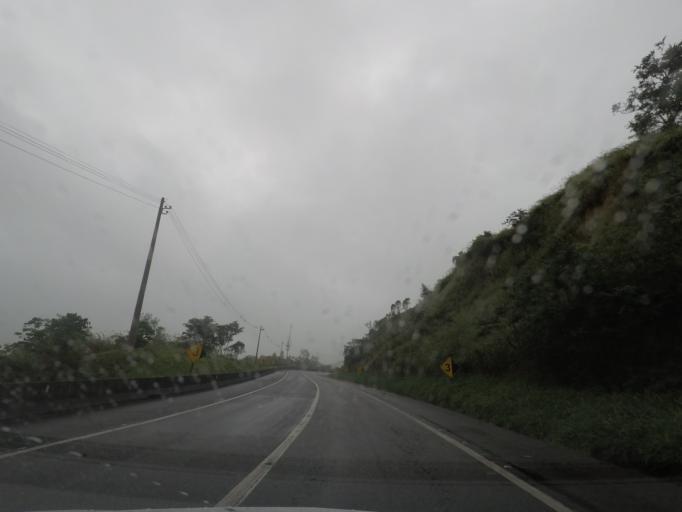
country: BR
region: Sao Paulo
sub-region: Cajati
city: Cajati
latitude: -24.9670
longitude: -48.4703
